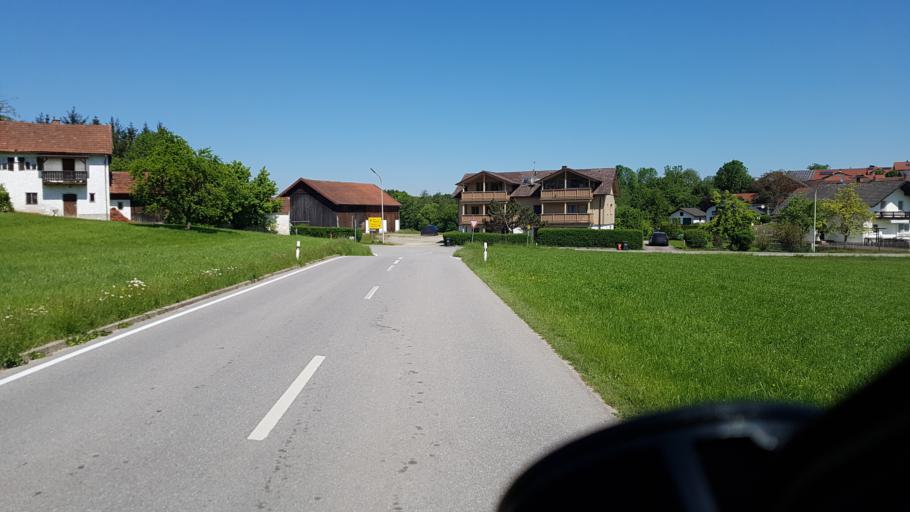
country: DE
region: Bavaria
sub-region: Lower Bavaria
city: Reut
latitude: 48.3414
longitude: 12.9199
